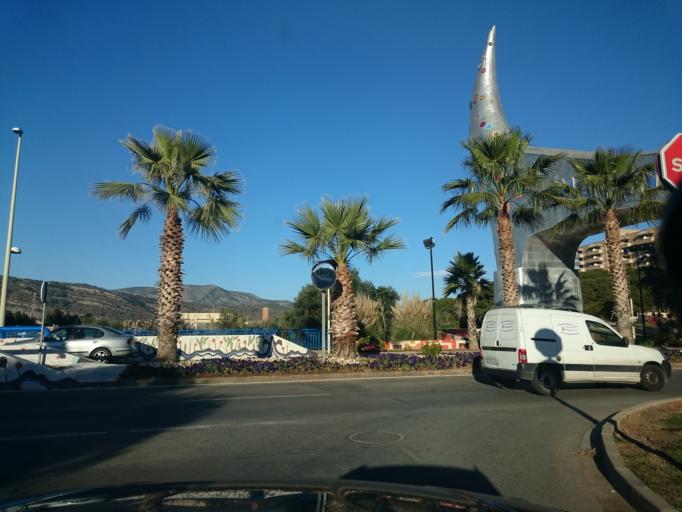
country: ES
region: Valencia
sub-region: Provincia de Castello
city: Orpesa/Oropesa del Mar
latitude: 40.1069
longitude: 0.1489
